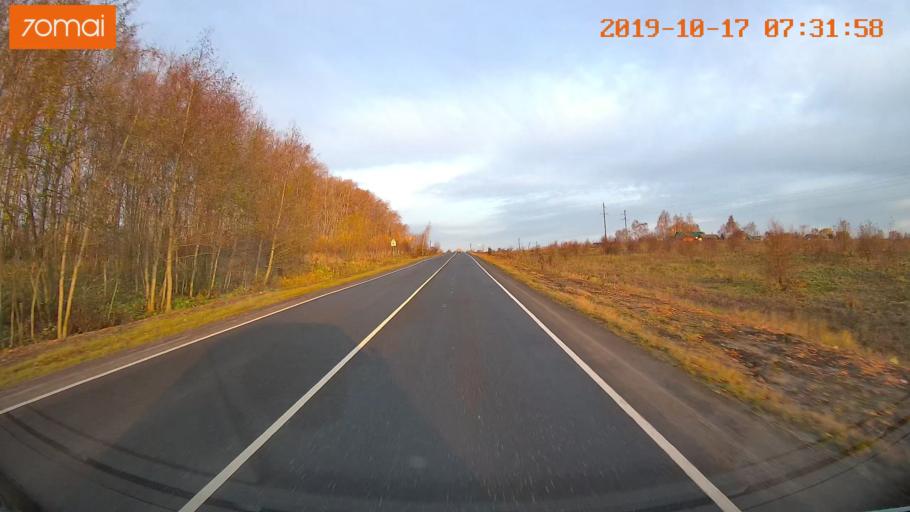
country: RU
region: Ivanovo
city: Gavrilov Posad
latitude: 56.3944
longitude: 39.9849
